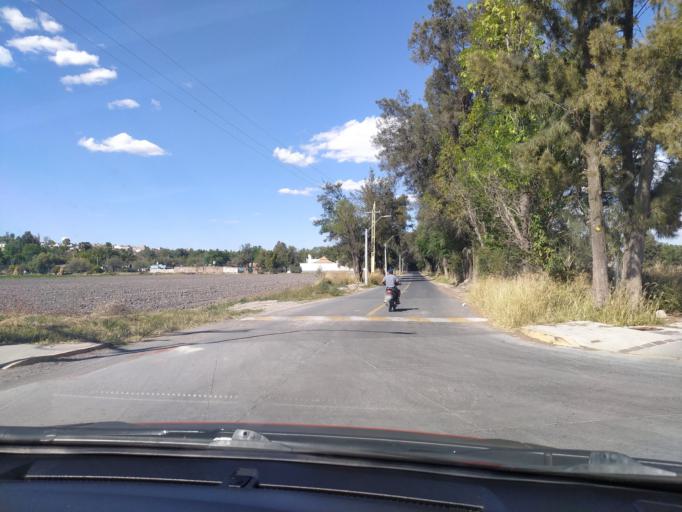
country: LA
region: Oudomxai
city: Muang La
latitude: 21.0400
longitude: 101.8378
